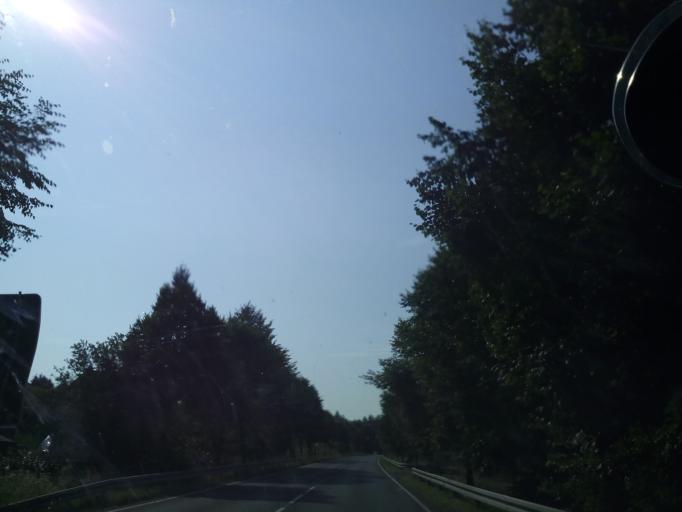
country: DE
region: Hesse
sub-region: Regierungsbezirk Kassel
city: Hilders
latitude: 50.5694
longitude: 10.0023
